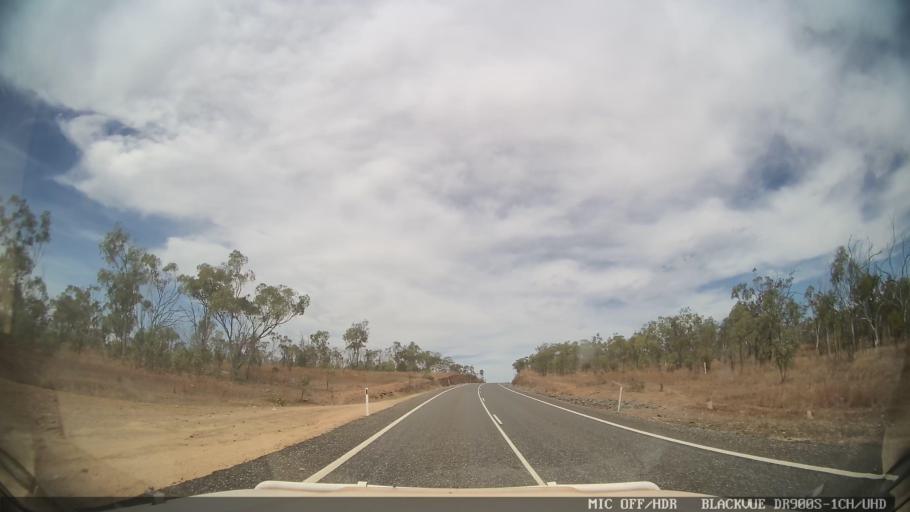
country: AU
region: Queensland
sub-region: Cairns
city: Port Douglas
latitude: -16.4406
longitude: 144.7869
